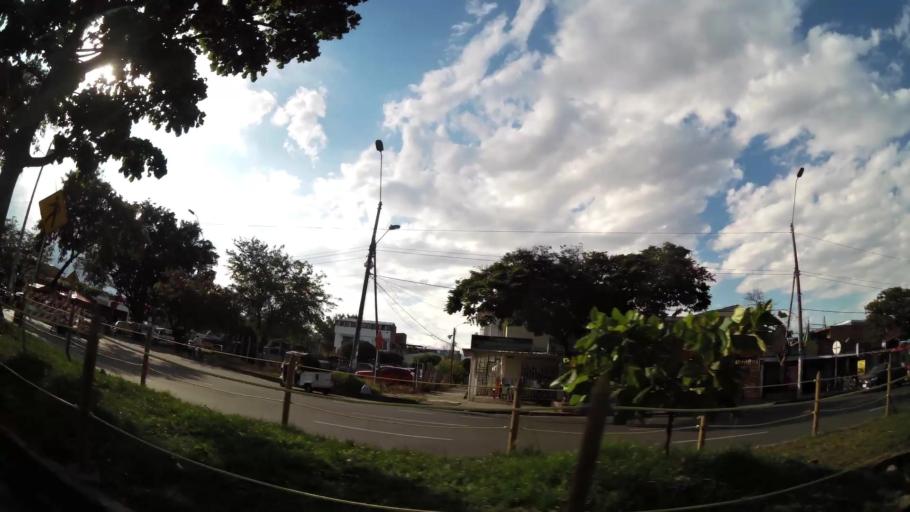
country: CO
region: Valle del Cauca
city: Cali
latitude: 3.3989
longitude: -76.5076
